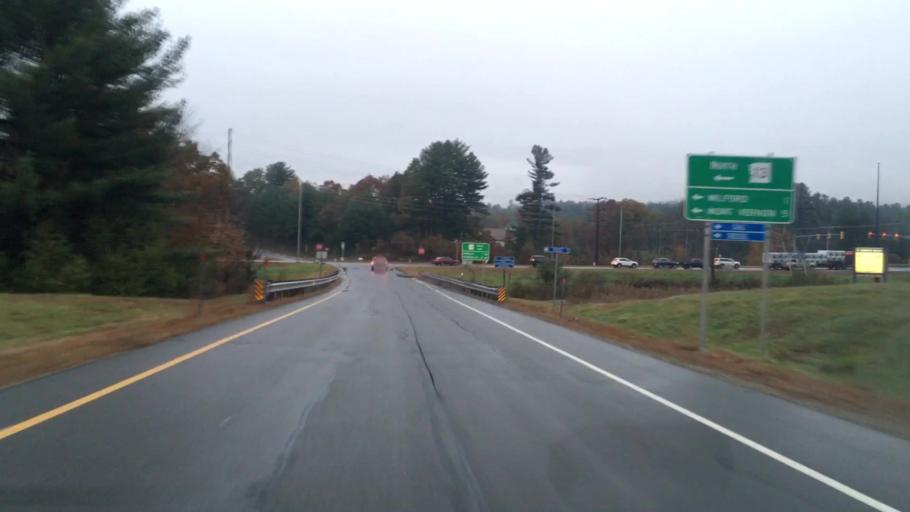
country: US
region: New Hampshire
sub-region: Hillsborough County
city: Milford
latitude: 42.8168
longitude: -71.6479
